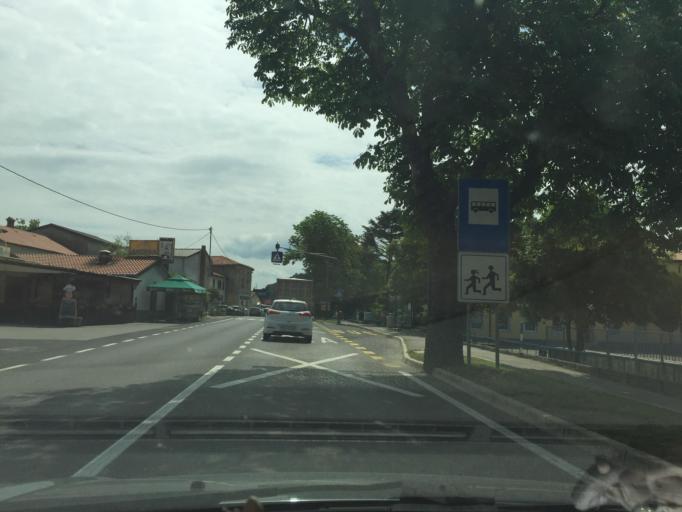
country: SI
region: Hrpelje-Kozina
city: Kozina
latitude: 45.6061
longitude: 13.9455
